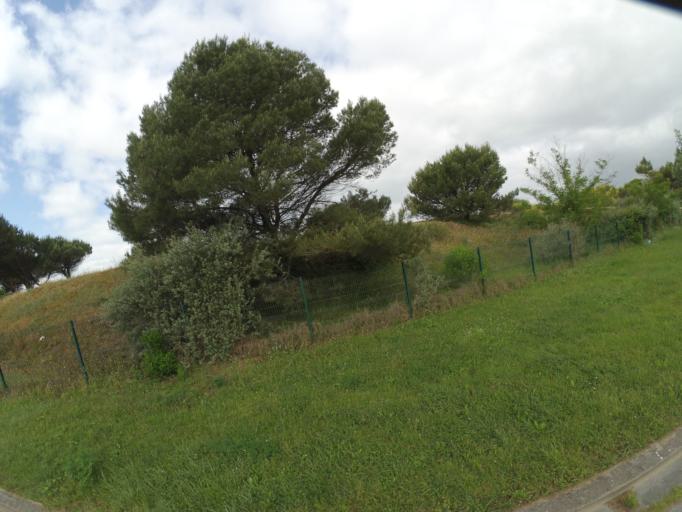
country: FR
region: Poitou-Charentes
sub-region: Departement de la Charente-Maritime
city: Angoulins
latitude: 46.1146
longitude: -1.1232
